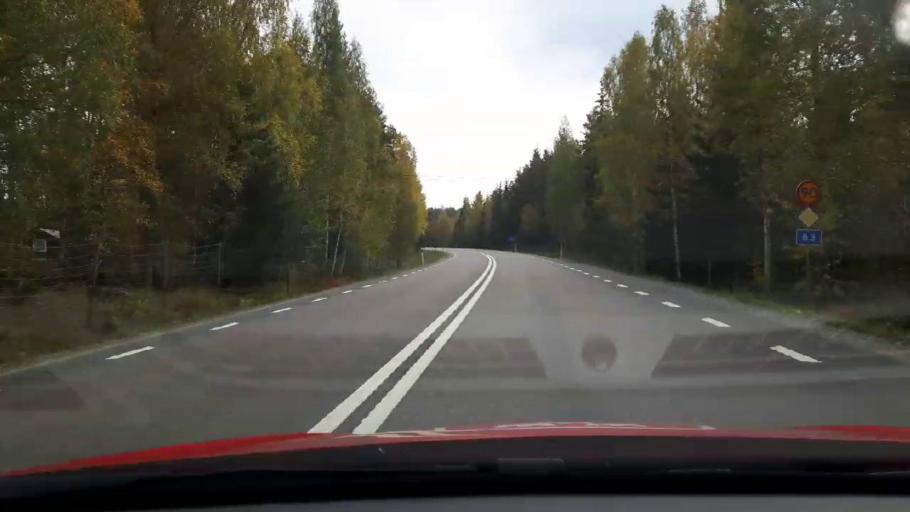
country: SE
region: Gaevleborg
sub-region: Bollnas Kommun
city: Kilafors
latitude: 61.2747
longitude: 16.5271
